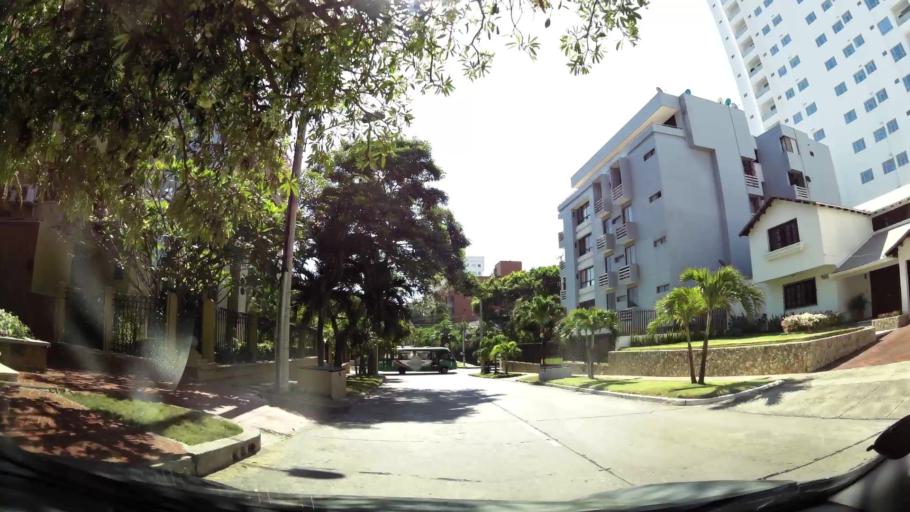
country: CO
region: Atlantico
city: Barranquilla
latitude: 11.0140
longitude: -74.8188
